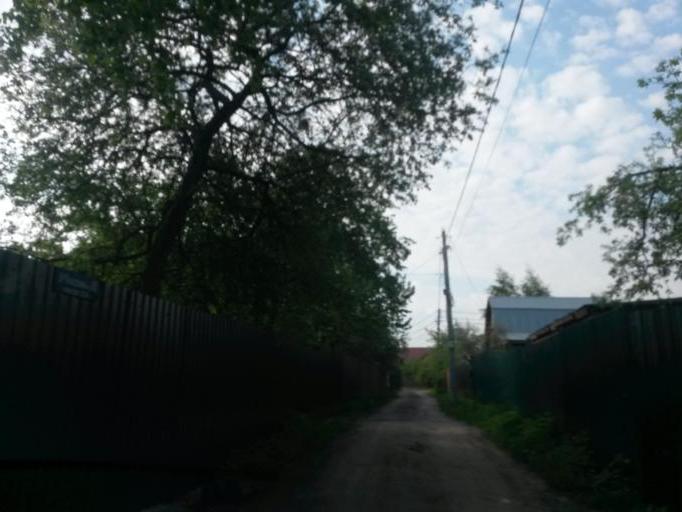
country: RU
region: Moscow
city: Zyablikovo
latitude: 55.5927
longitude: 37.7681
